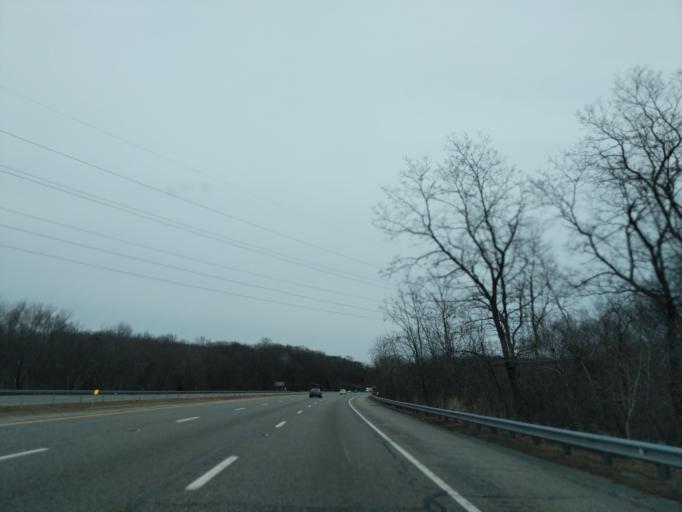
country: US
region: Rhode Island
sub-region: Providence County
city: Cumberland
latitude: 41.9506
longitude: -71.4234
